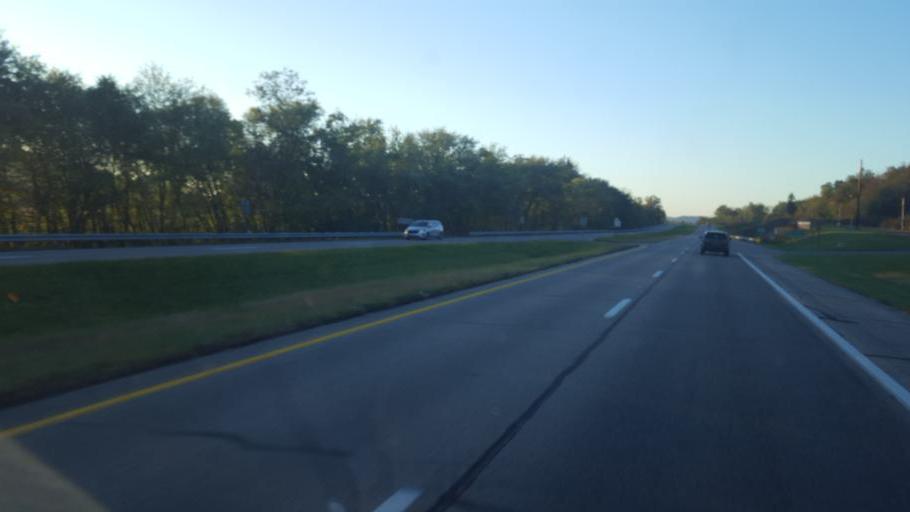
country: US
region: Ohio
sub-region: Scioto County
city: Lucasville
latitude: 38.9110
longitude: -83.0112
